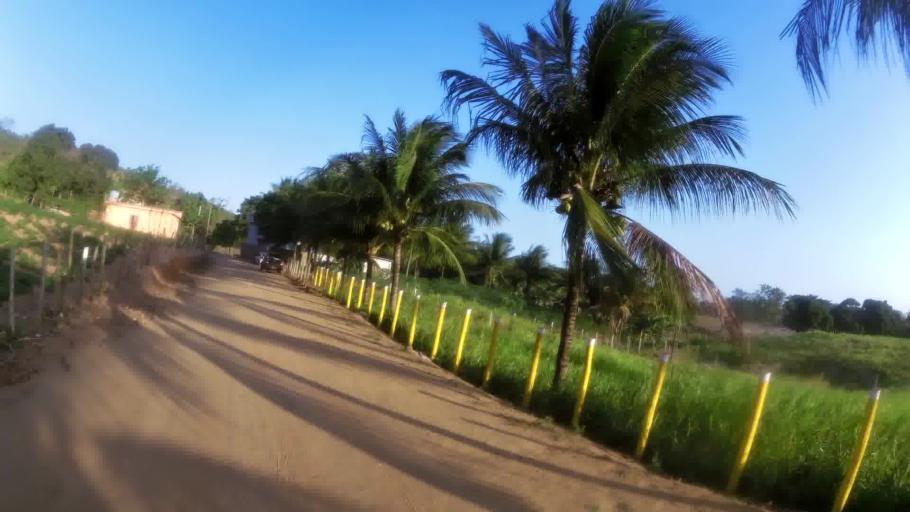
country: BR
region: Espirito Santo
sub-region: Piuma
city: Piuma
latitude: -20.8829
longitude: -40.7831
